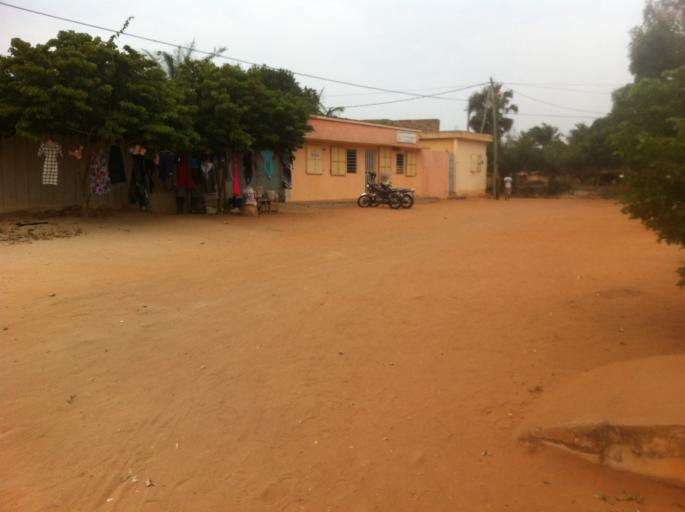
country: TG
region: Maritime
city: Lome
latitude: 6.1852
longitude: 1.2052
